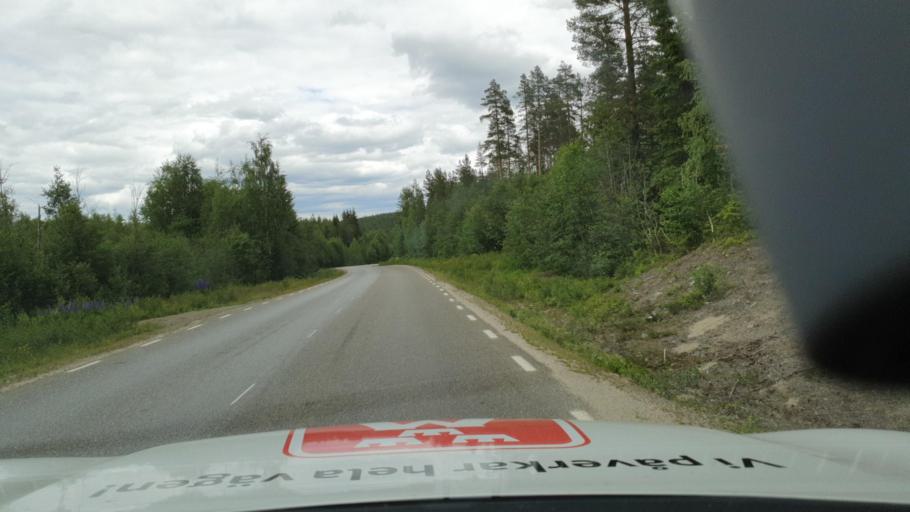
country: SE
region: Vaesterbotten
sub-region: Bjurholms Kommun
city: Bjurholm
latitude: 63.8677
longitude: 18.9696
